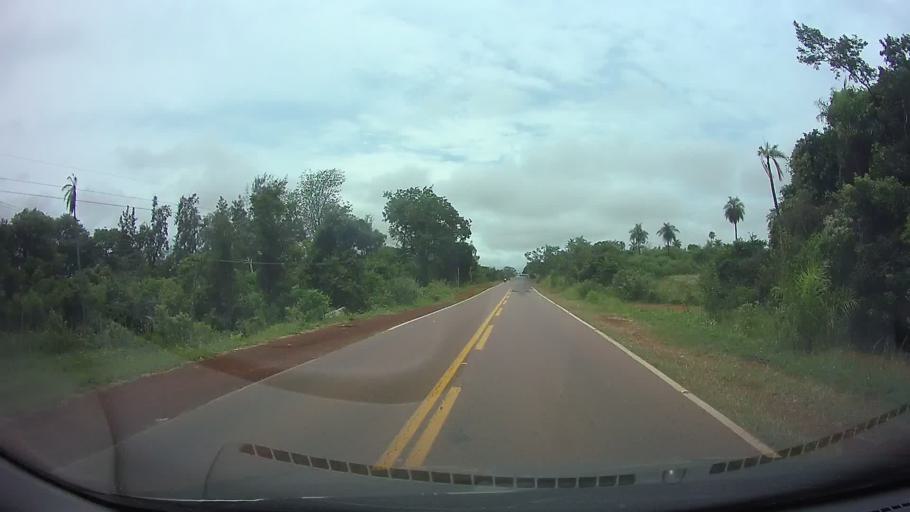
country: PY
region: Paraguari
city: Acahay
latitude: -25.8553
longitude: -57.1382
